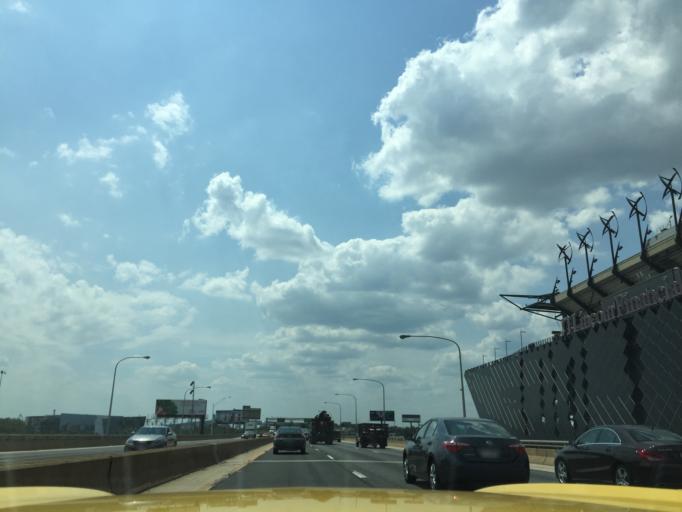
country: US
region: New Jersey
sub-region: Gloucester County
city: National Park
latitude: 39.8993
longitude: -75.1659
